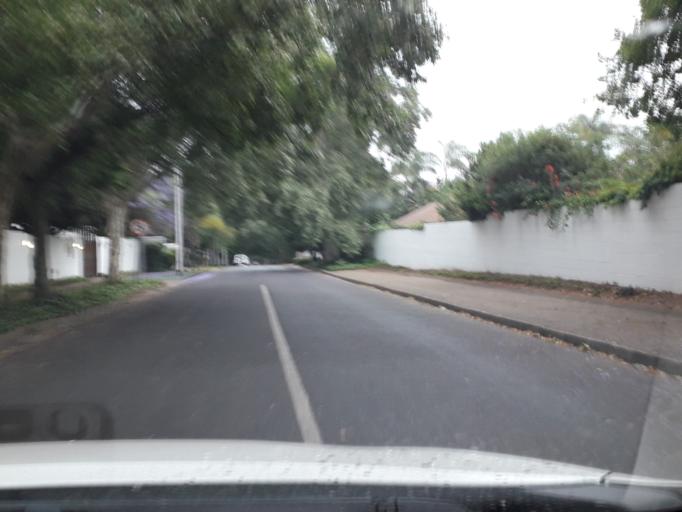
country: ZA
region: Gauteng
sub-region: City of Johannesburg Metropolitan Municipality
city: Johannesburg
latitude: -26.1387
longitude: 28.0472
